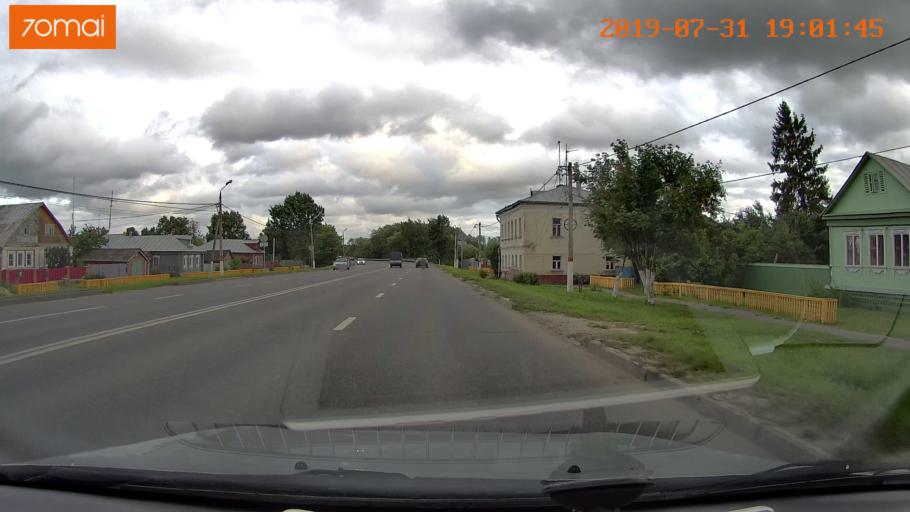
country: RU
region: Moskovskaya
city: Raduzhnyy
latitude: 55.1243
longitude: 38.7294
